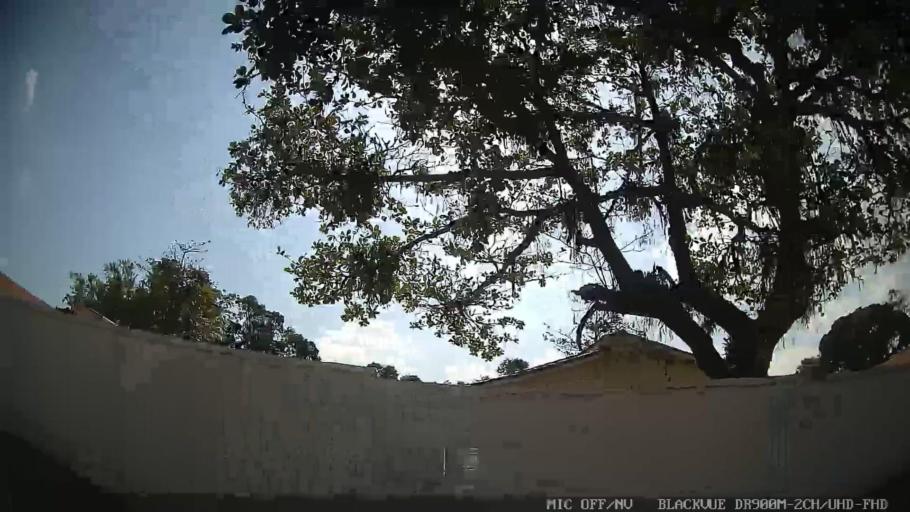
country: BR
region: Sao Paulo
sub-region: Santos
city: Santos
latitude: -23.9390
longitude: -46.2999
